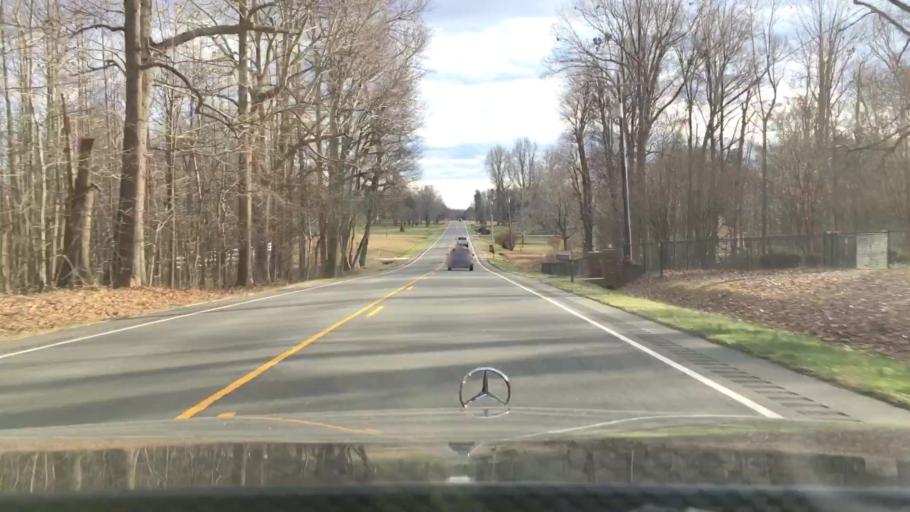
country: US
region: North Carolina
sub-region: Orange County
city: Hillsborough
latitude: 36.1837
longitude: -79.1371
